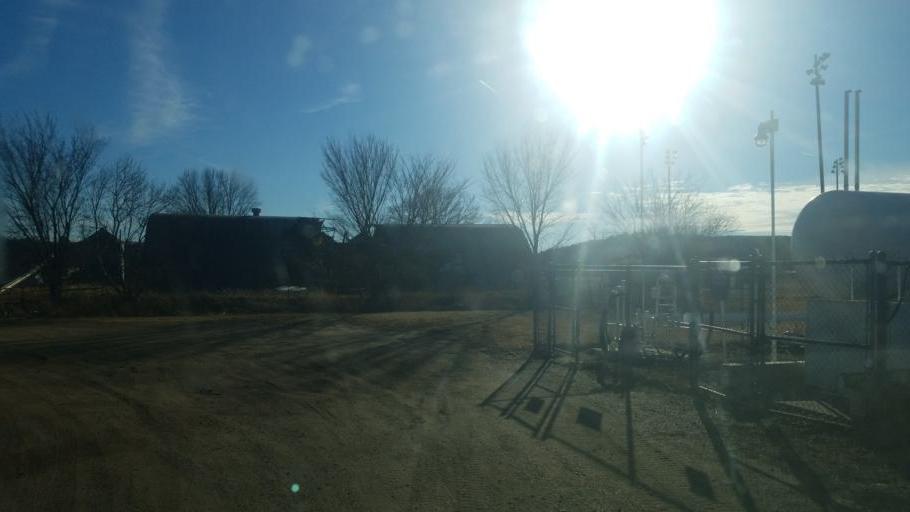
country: US
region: South Dakota
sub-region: Charles Mix County
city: Wagner
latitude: 42.8287
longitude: -98.4697
